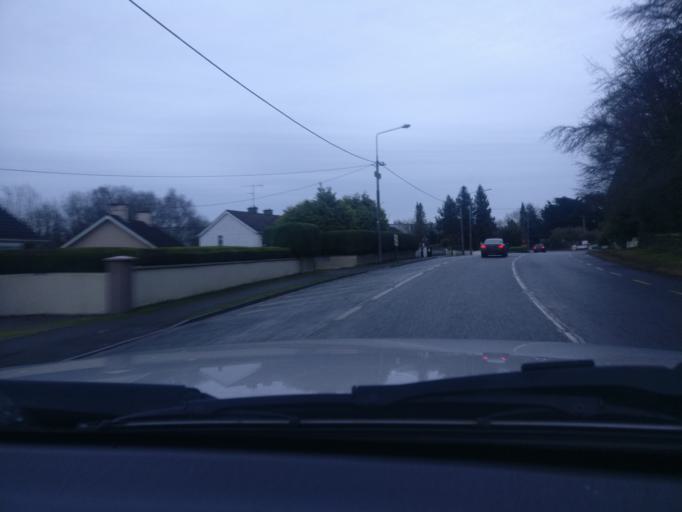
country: IE
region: Leinster
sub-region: An Mhi
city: Navan
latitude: 53.6560
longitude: -6.7049
